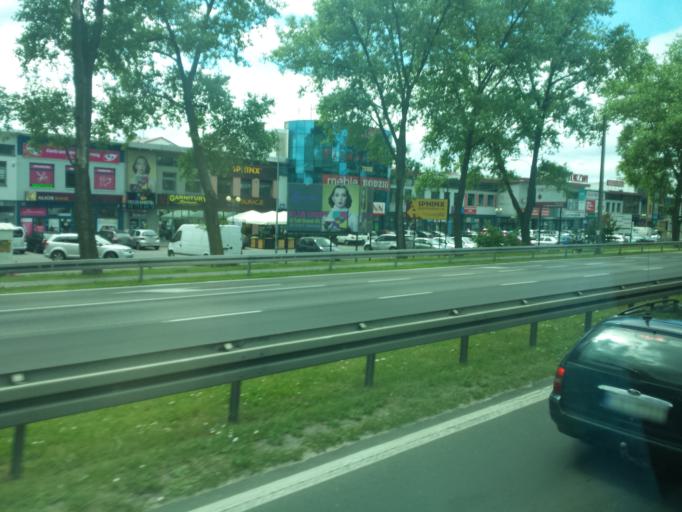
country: PL
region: Masovian Voivodeship
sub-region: Warszawa
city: Wesola
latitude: 52.2234
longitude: 21.2337
